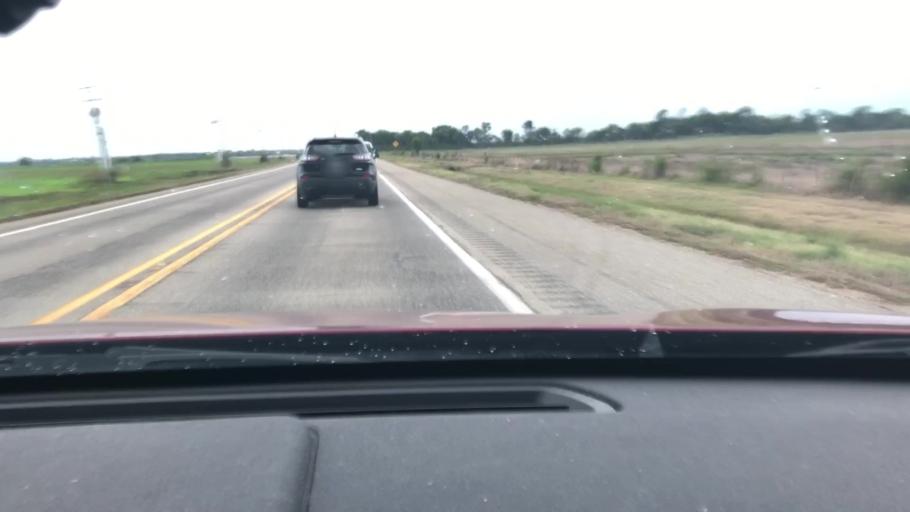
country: US
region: Arkansas
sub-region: Lafayette County
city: Lewisville
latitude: 33.4017
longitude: -93.7445
